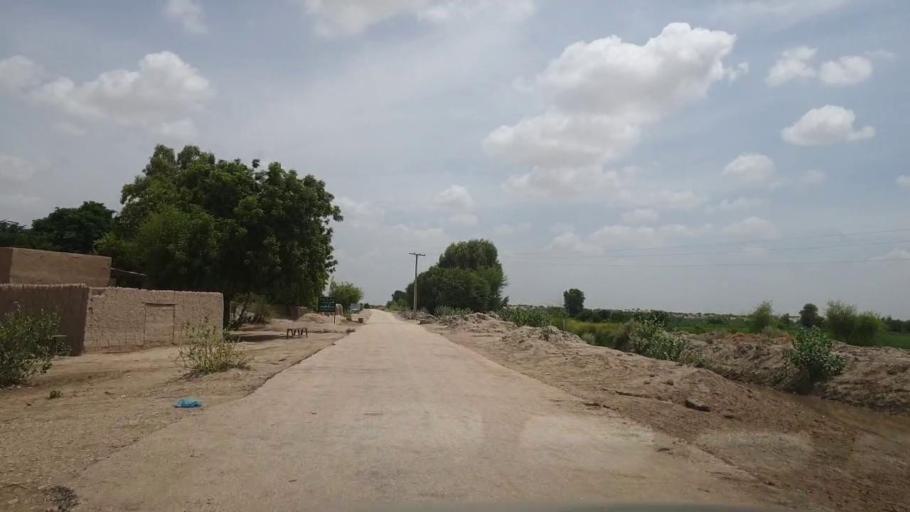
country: PK
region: Sindh
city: Kot Diji
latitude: 27.2076
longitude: 69.1170
